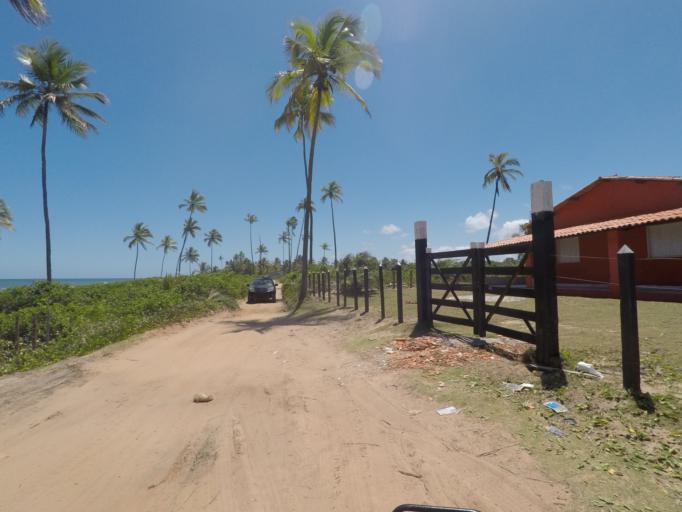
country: BR
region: Bahia
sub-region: Marau
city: Marau
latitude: -14.0193
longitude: -38.9459
